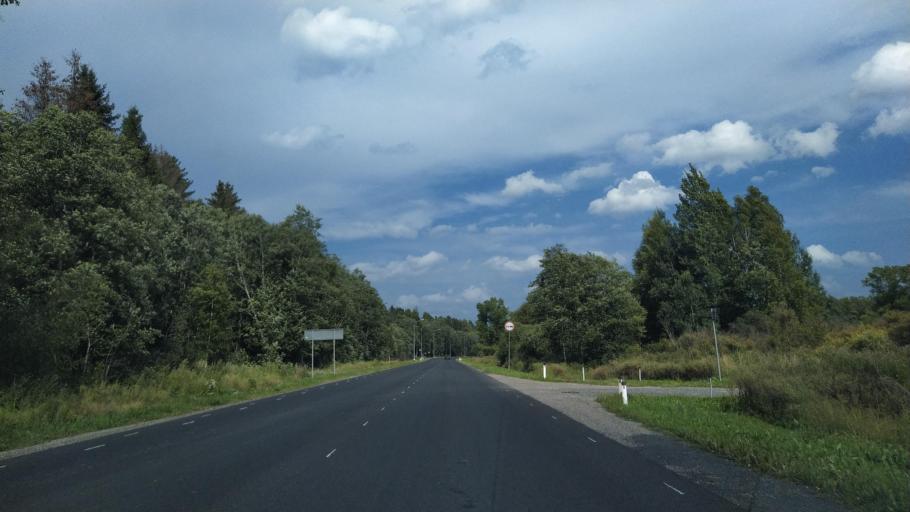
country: RU
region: Pskov
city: Vybor
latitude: 57.7256
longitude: 28.9599
